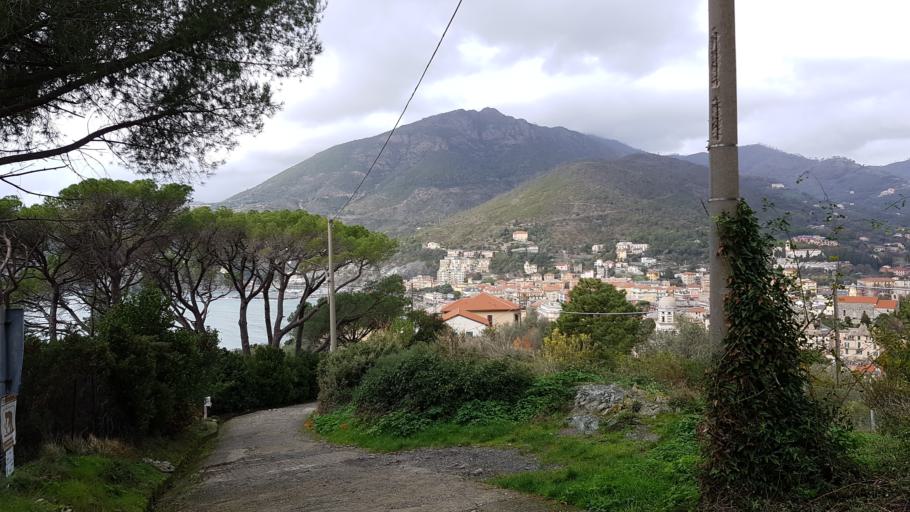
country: IT
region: Liguria
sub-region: Provincia di La Spezia
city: Levanto
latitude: 44.1642
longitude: 9.6120
